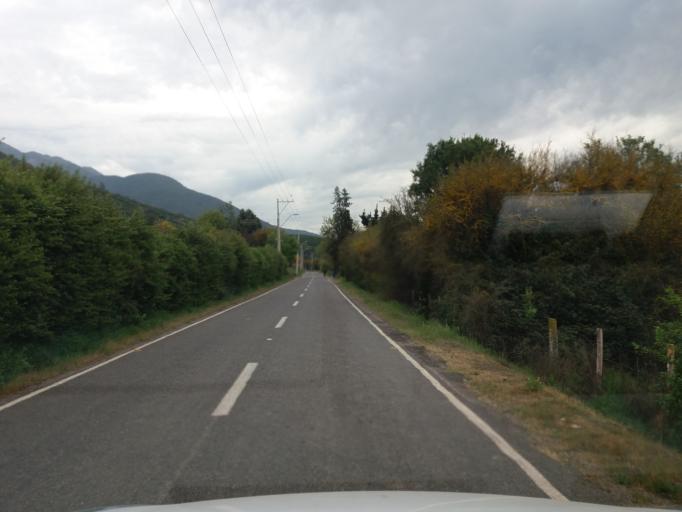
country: CL
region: Valparaiso
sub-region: Provincia de Quillota
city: Quillota
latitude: -32.9048
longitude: -71.1036
